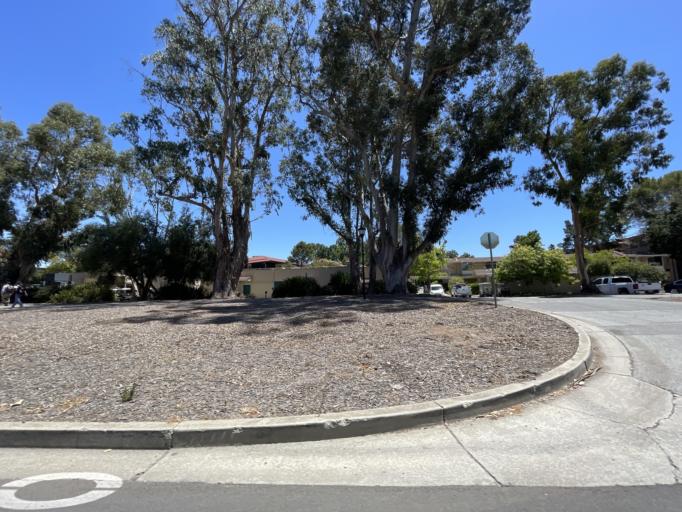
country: US
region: California
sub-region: Santa Clara County
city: Stanford
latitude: 37.4294
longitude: -122.1783
